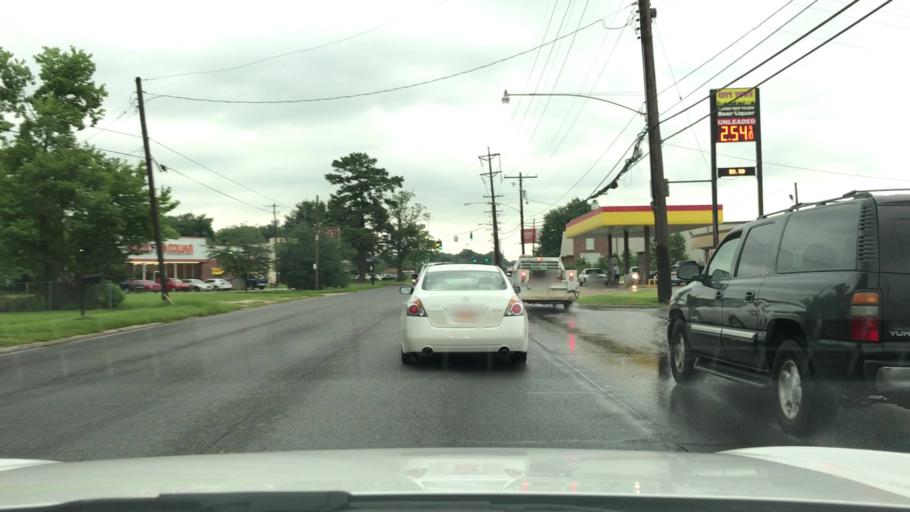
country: US
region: Louisiana
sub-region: East Baton Rouge Parish
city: Merrydale
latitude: 30.4742
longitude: -91.1184
